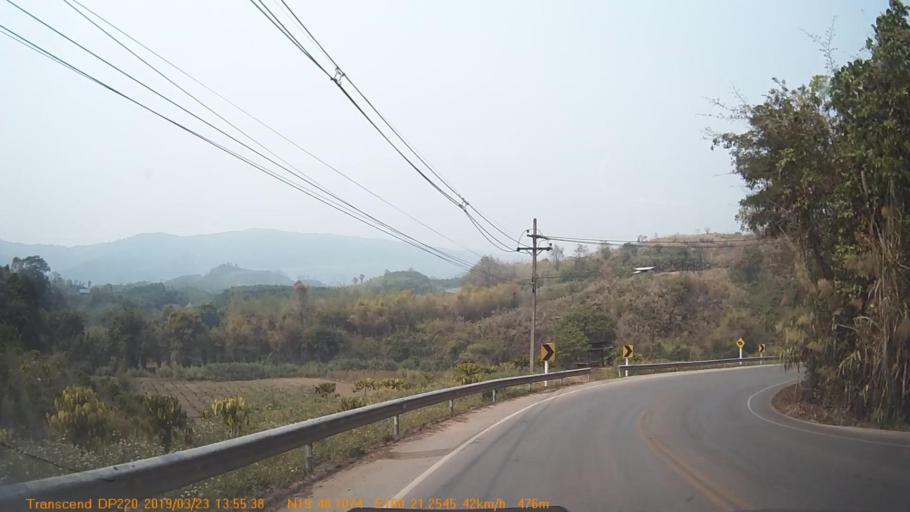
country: TH
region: Chiang Rai
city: Khun Tan
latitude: 19.8022
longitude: 100.3546
